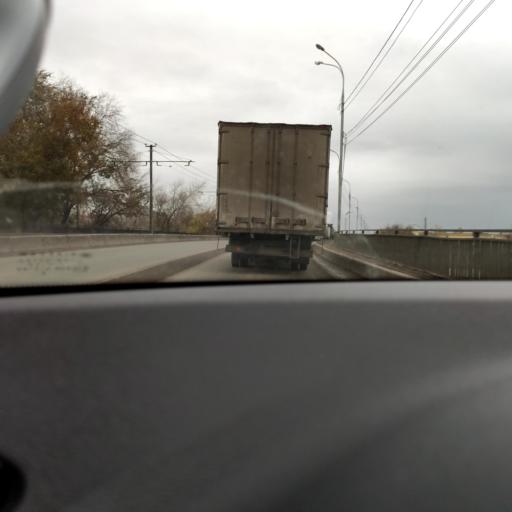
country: RU
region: Samara
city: Smyshlyayevka
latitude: 53.2165
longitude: 50.2913
